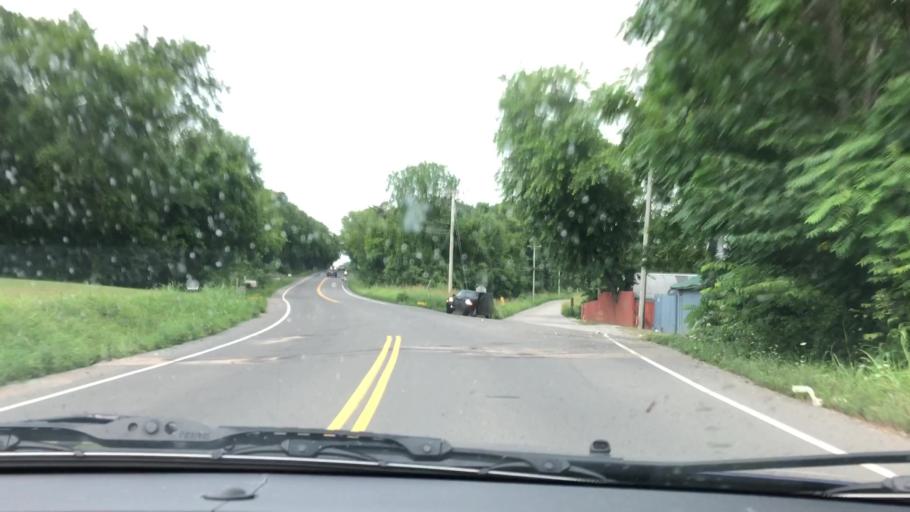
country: US
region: Tennessee
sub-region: Williamson County
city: Franklin
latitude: 35.8966
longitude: -86.9178
